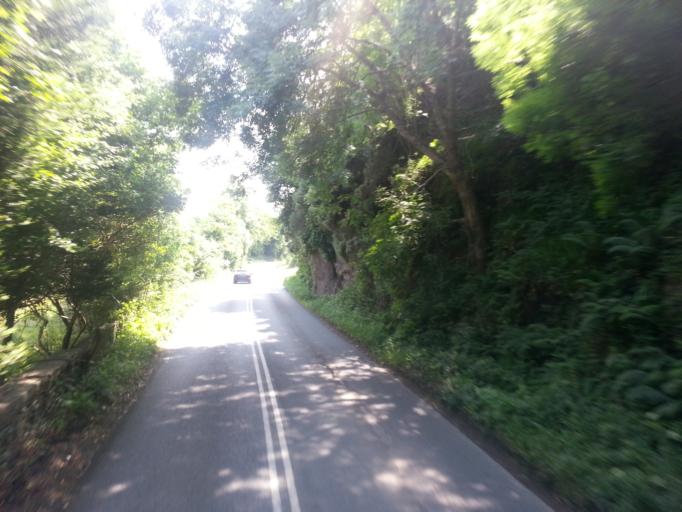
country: IE
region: Leinster
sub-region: Wicklow
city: Enniskerry
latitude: 53.2159
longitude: -6.1787
